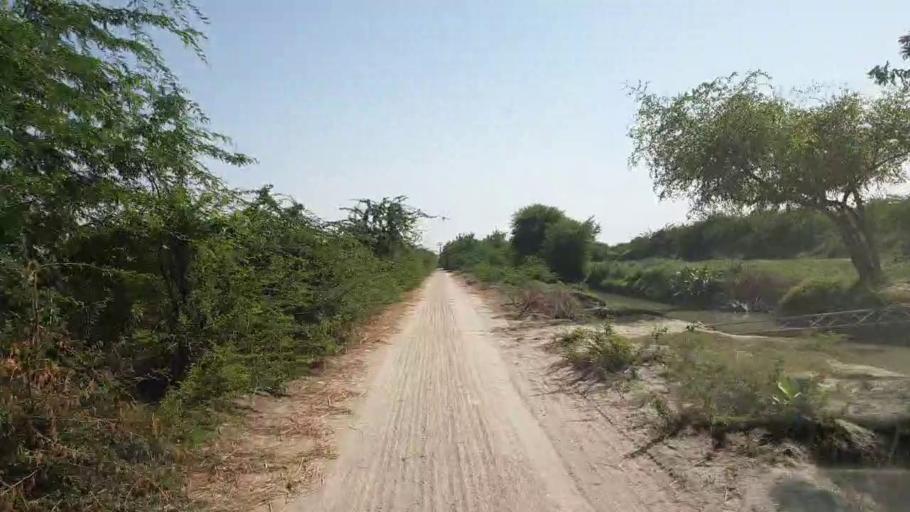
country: PK
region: Sindh
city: Tando Bago
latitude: 24.6474
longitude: 68.9855
